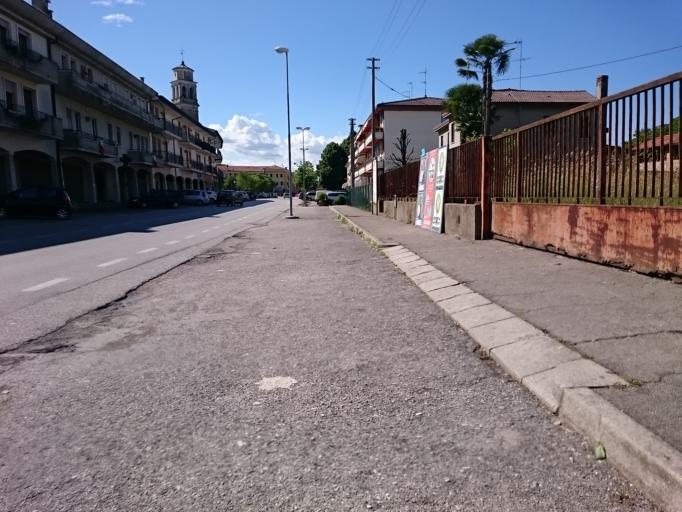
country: IT
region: Veneto
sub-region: Provincia di Venezia
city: Campolongo Maggiore Liettoli
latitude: 45.3446
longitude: 12.0092
